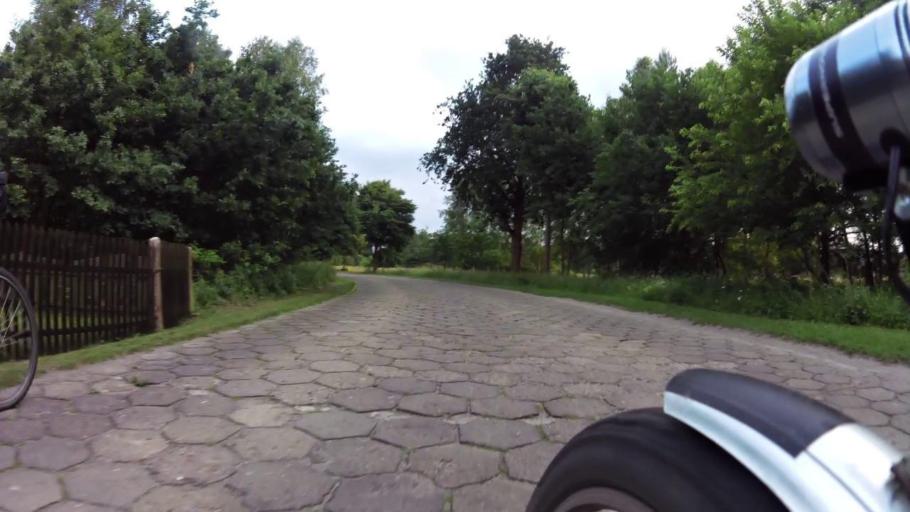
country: PL
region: West Pomeranian Voivodeship
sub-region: Powiat policki
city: Police
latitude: 53.6561
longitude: 14.4953
